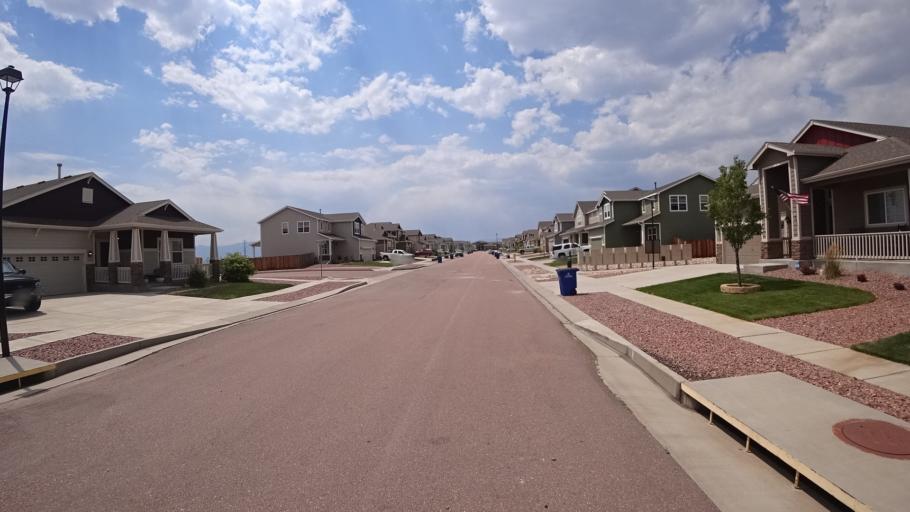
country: US
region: Colorado
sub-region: El Paso County
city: Black Forest
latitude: 38.9442
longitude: -104.6867
